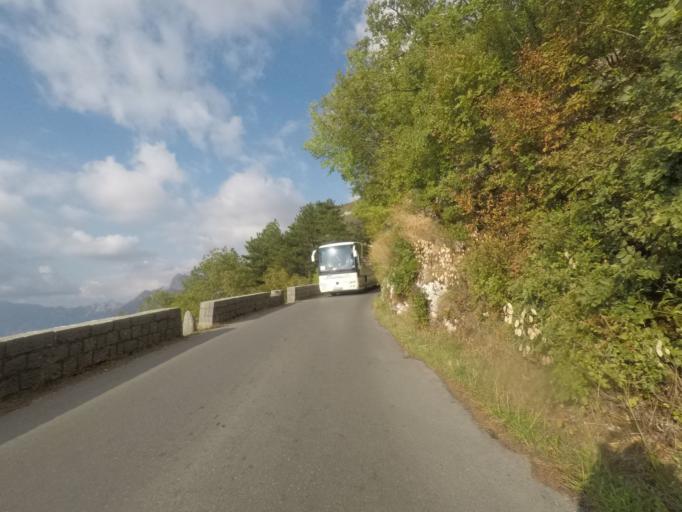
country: ME
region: Kotor
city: Kotor
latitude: 42.4035
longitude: 18.7808
